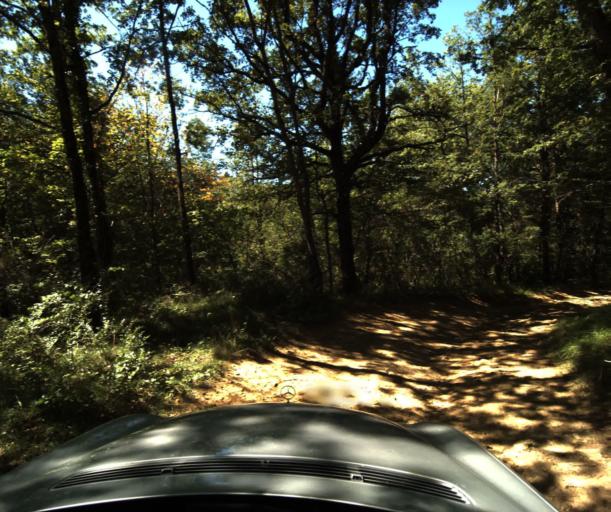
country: FR
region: Midi-Pyrenees
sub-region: Departement de l'Ariege
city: Belesta
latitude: 42.9696
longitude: 1.9250
